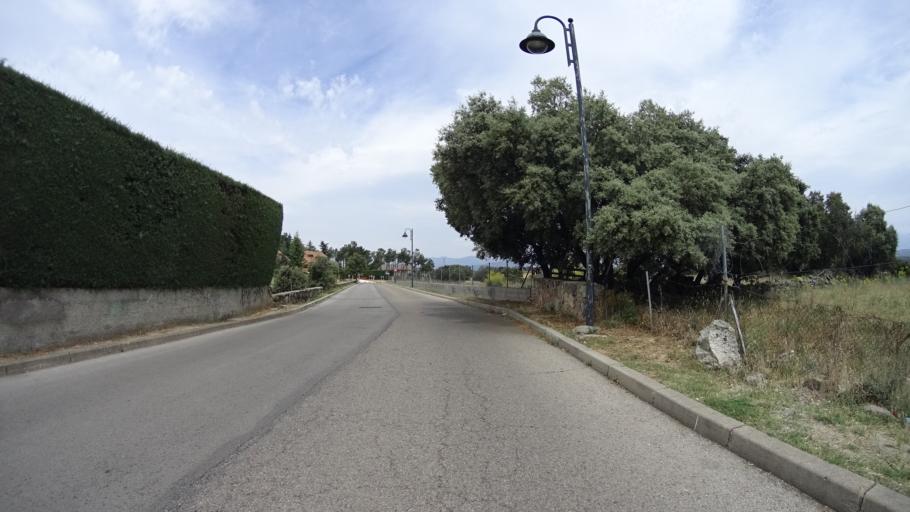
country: ES
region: Madrid
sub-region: Provincia de Madrid
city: Galapagar
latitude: 40.5696
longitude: -4.0062
